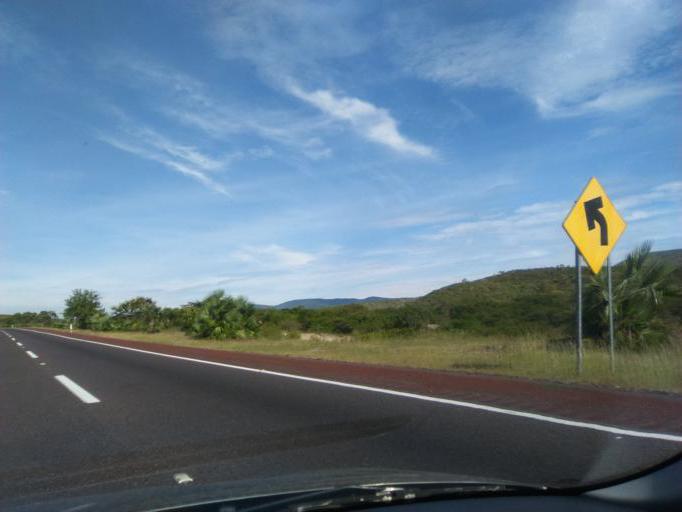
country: MX
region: Guerrero
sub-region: Huitzuco de los Figueroa
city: San Francisco Ozomatlan
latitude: 17.9796
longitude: -99.3209
